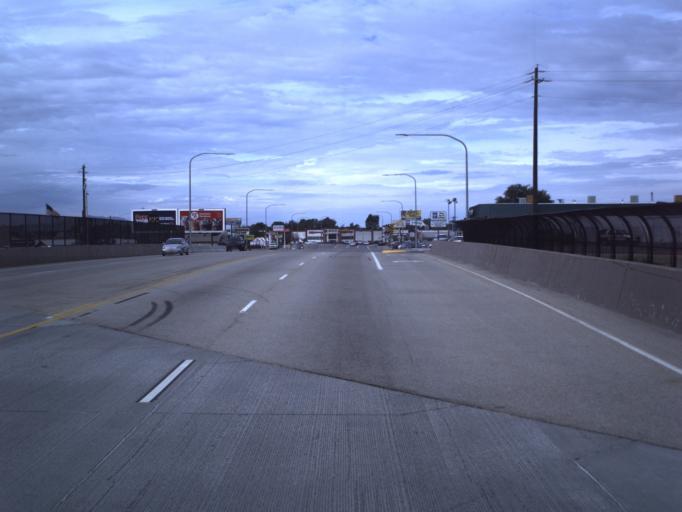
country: US
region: Utah
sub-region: Weber County
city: Roy
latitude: 41.1696
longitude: -112.0221
